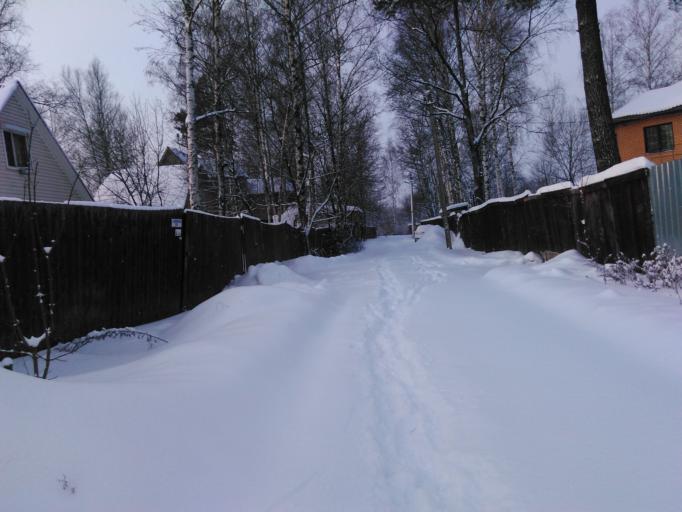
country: RU
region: Moskovskaya
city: Pravdinskiy
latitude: 56.0412
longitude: 37.8621
